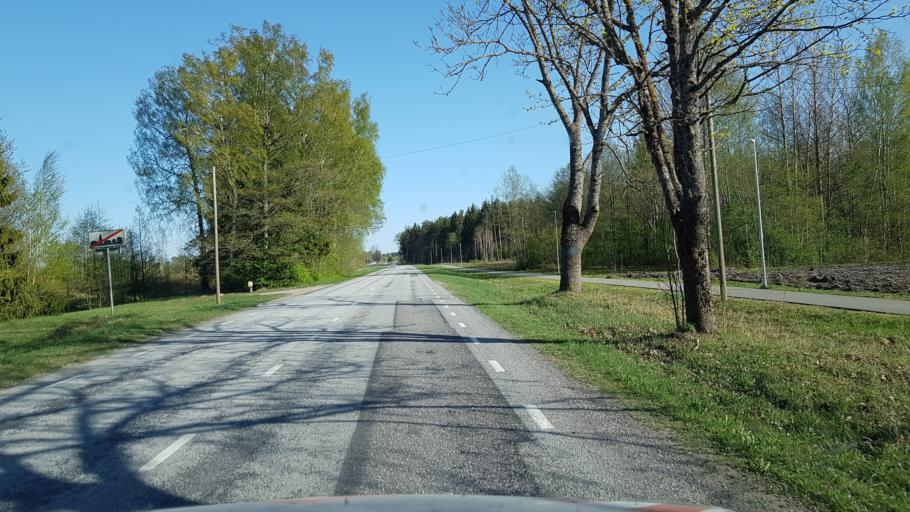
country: EE
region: Paernumaa
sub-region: Paikuse vald
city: Paikuse
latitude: 58.3682
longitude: 24.6374
